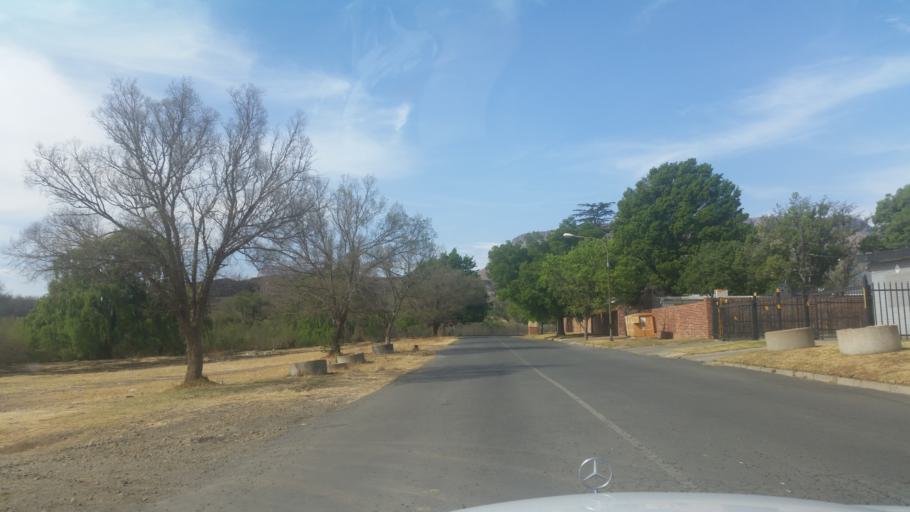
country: ZA
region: Orange Free State
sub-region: Thabo Mofutsanyana District Municipality
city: Harrismith
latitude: -28.2631
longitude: 29.1188
